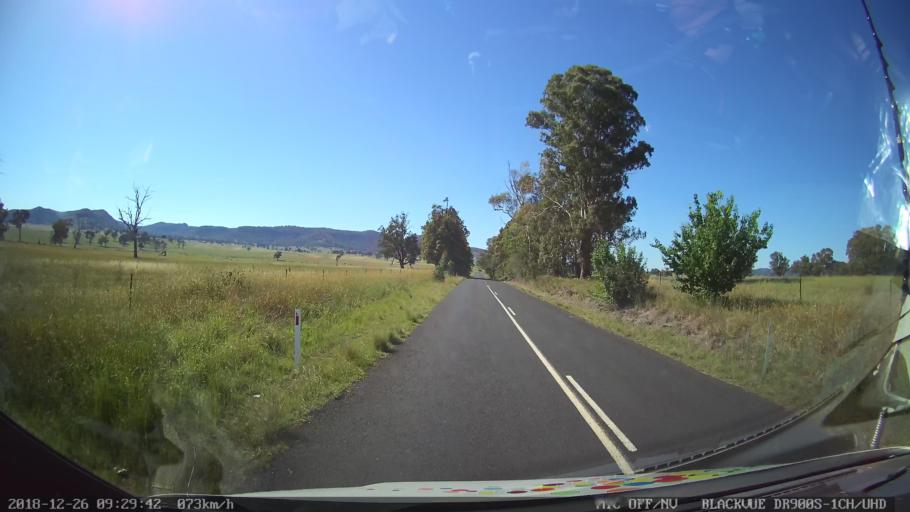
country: AU
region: New South Wales
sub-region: Mid-Western Regional
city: Kandos
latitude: -32.8557
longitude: 150.0286
